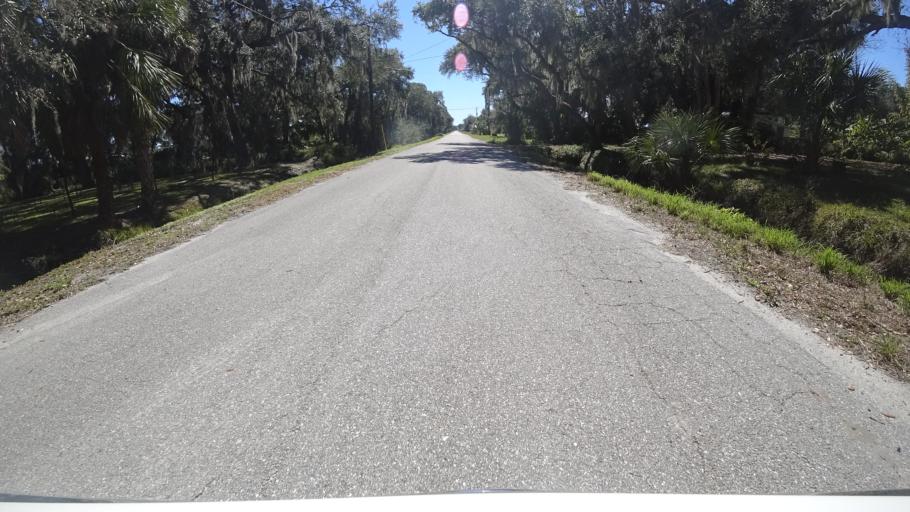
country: US
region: Florida
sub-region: Manatee County
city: Memphis
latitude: 27.5738
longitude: -82.5483
